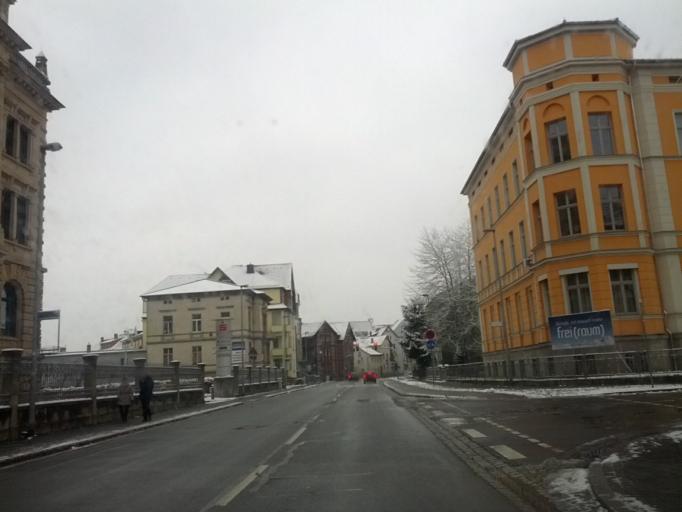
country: DE
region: Thuringia
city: Meiningen
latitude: 50.5751
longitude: 10.4161
